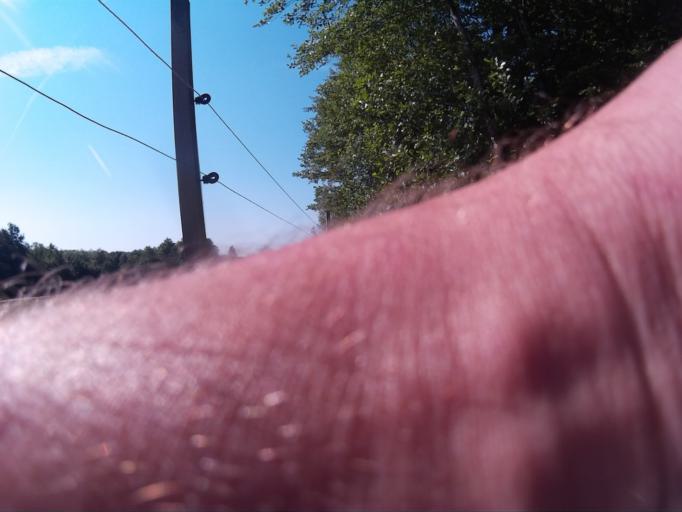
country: AT
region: Burgenland
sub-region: Politischer Bezirk Gussing
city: Heiligenbrunn
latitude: 46.9322
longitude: 16.4667
